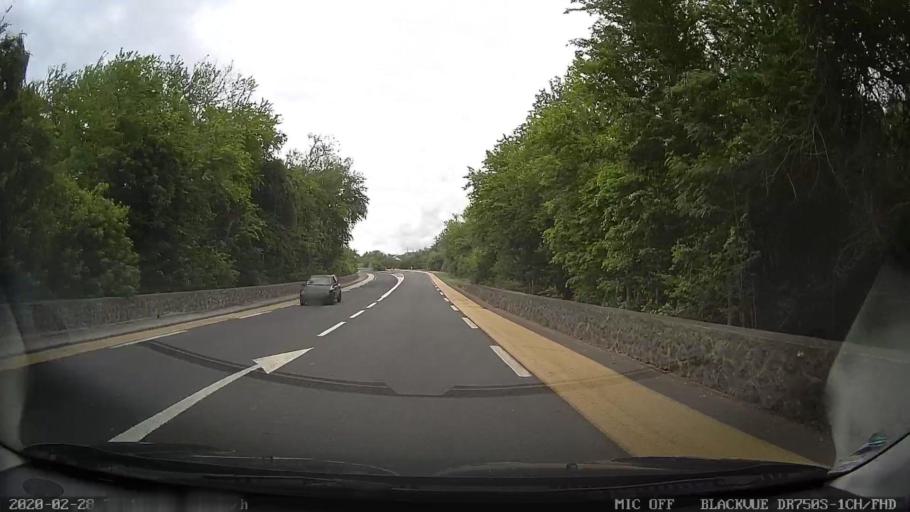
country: RE
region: Reunion
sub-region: Reunion
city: Trois-Bassins
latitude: -21.1196
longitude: 55.2606
